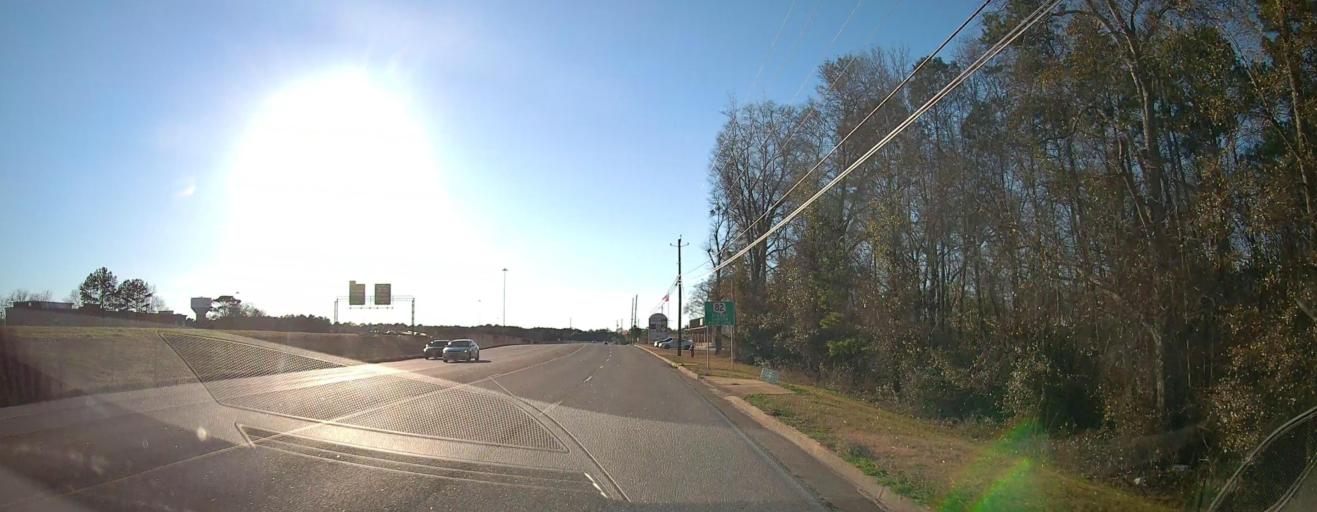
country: US
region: Georgia
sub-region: Dougherty County
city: Albany
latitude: 31.6235
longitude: -84.2251
